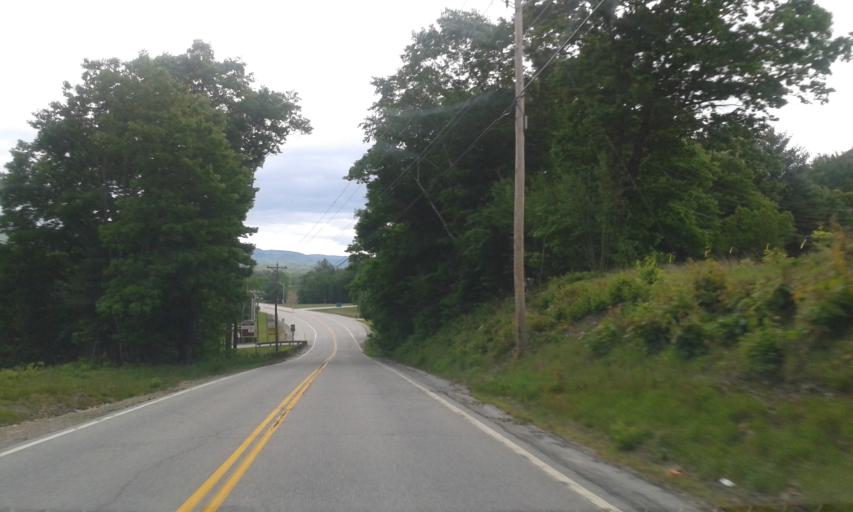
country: US
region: New Hampshire
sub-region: Grafton County
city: Woodstock
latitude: 43.9635
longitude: -71.6850
